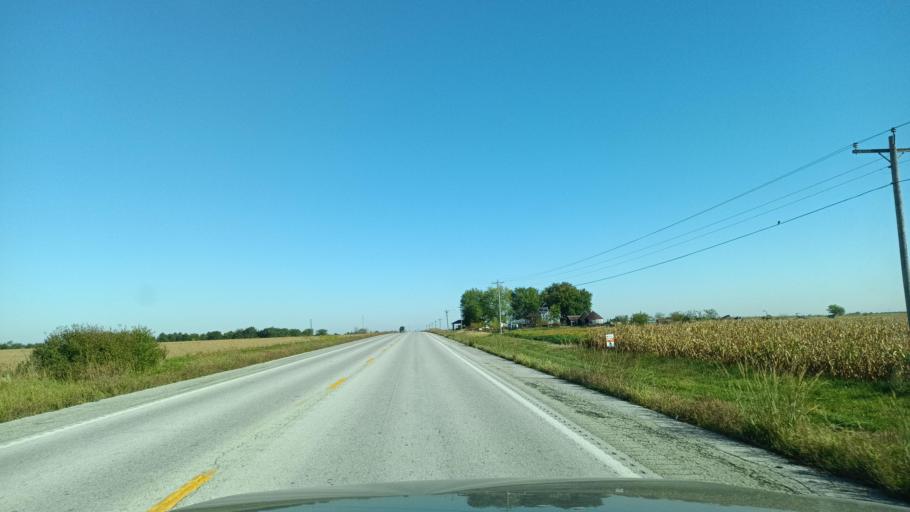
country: US
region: Missouri
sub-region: Audrain County
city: Vandalia
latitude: 39.4014
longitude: -91.6416
